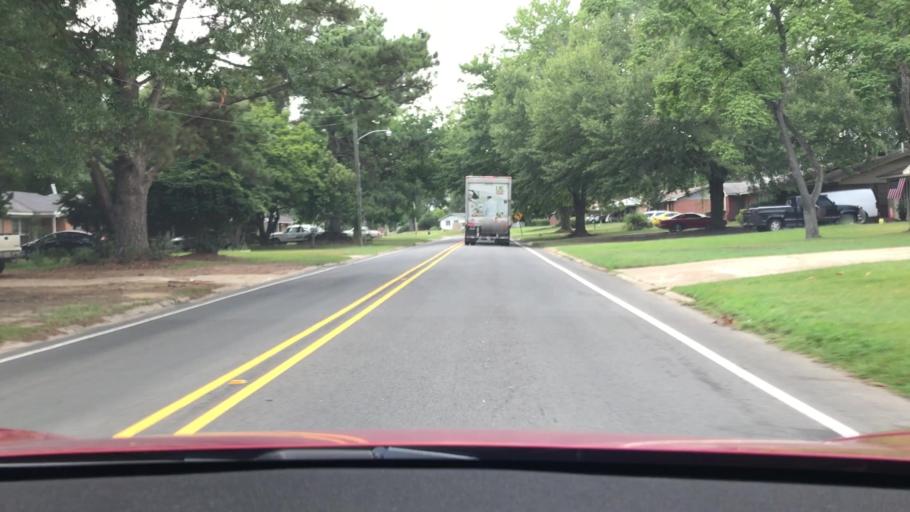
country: US
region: Louisiana
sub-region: De Soto Parish
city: Stonewall
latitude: 32.3954
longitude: -93.8011
